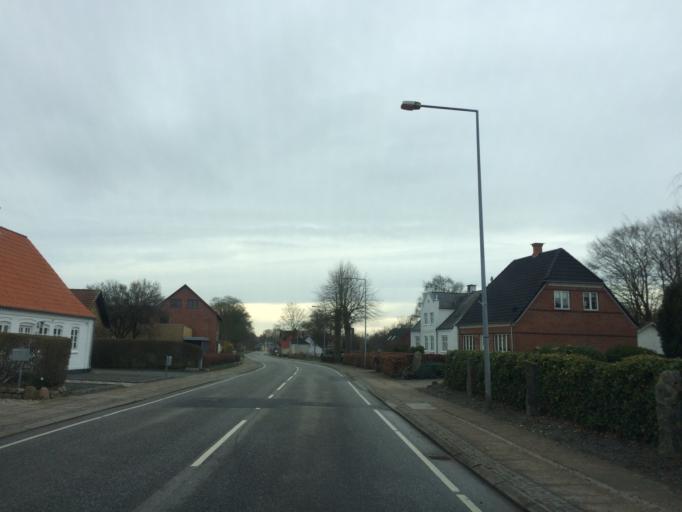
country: DK
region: South Denmark
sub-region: Assens Kommune
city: Assens
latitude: 55.2432
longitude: 9.9748
